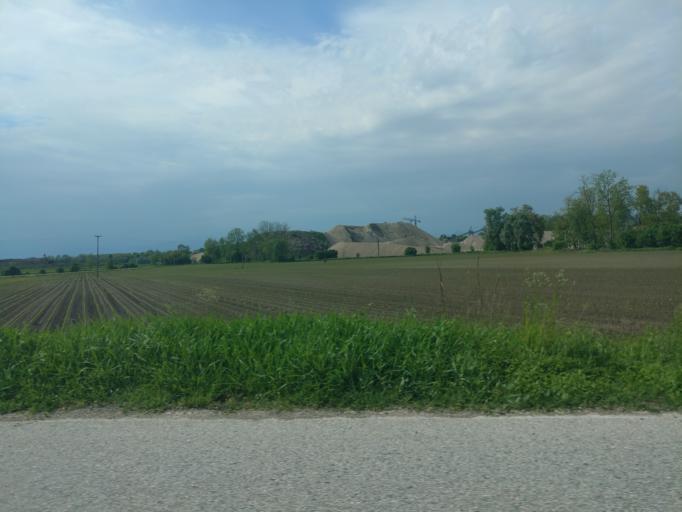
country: IT
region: Piedmont
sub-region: Provincia di Cuneo
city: Faule
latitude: 44.8088
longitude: 7.5826
